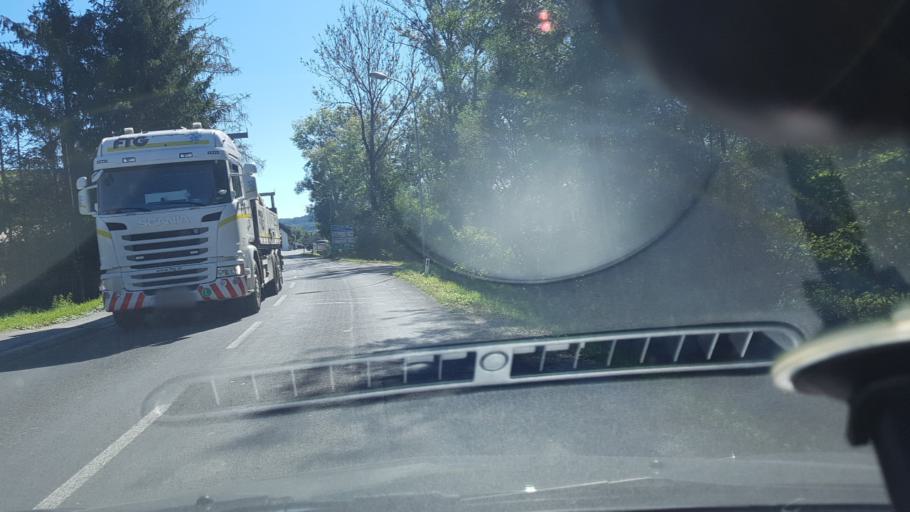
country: AT
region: Styria
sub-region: Politischer Bezirk Weiz
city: Sinabelkirchen
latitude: 47.1062
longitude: 15.8245
